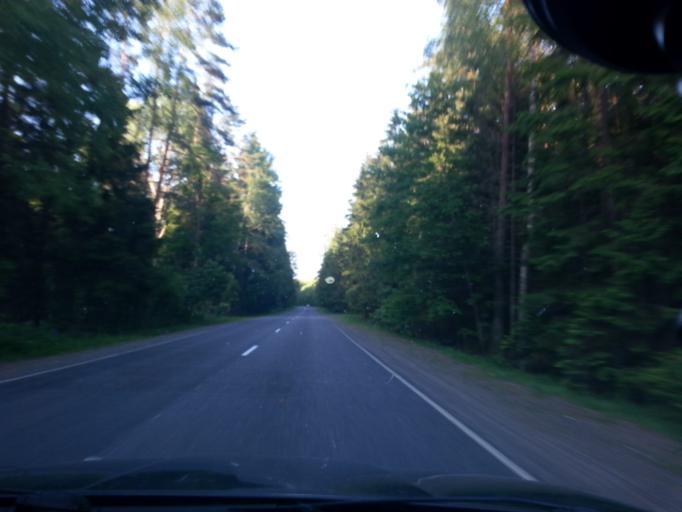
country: BY
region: Minsk
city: Narach
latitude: 54.9304
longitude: 26.5539
